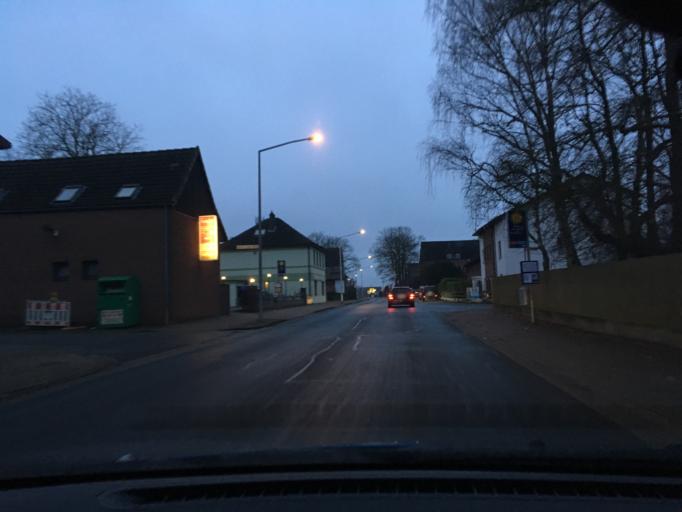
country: DE
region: Lower Saxony
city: Lehrte
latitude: 52.3617
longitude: 9.9110
